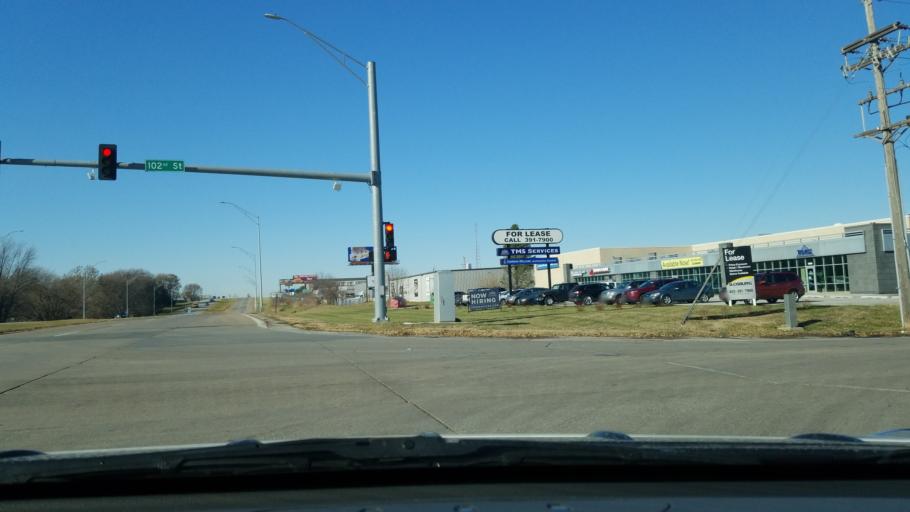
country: US
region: Nebraska
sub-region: Douglas County
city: Ralston
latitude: 41.2126
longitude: -96.0717
